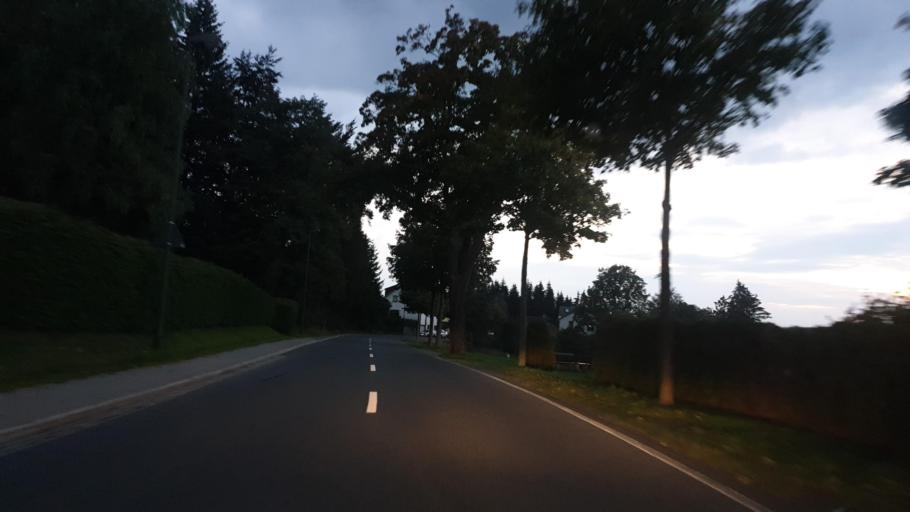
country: DE
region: Saxony
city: Rodewisch
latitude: 50.5065
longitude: 12.4599
